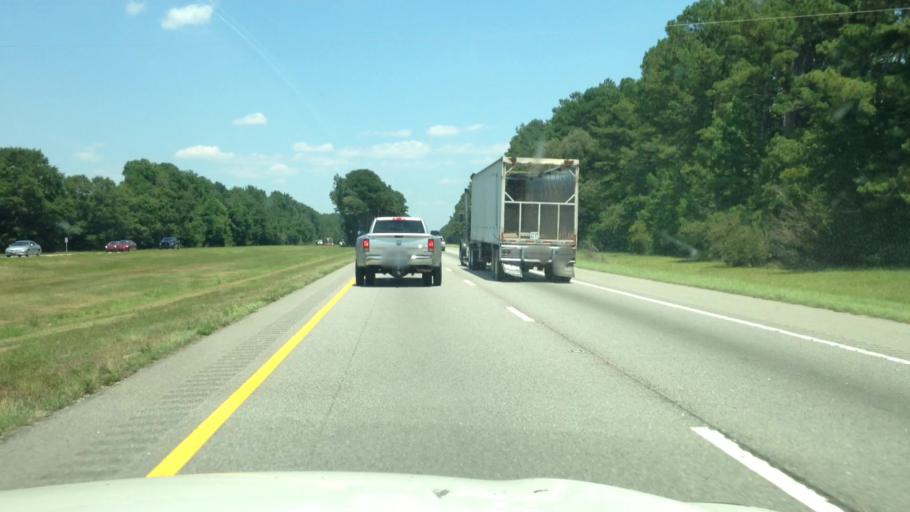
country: US
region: North Carolina
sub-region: Robeson County
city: Rowland
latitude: 34.5445
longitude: -79.2205
